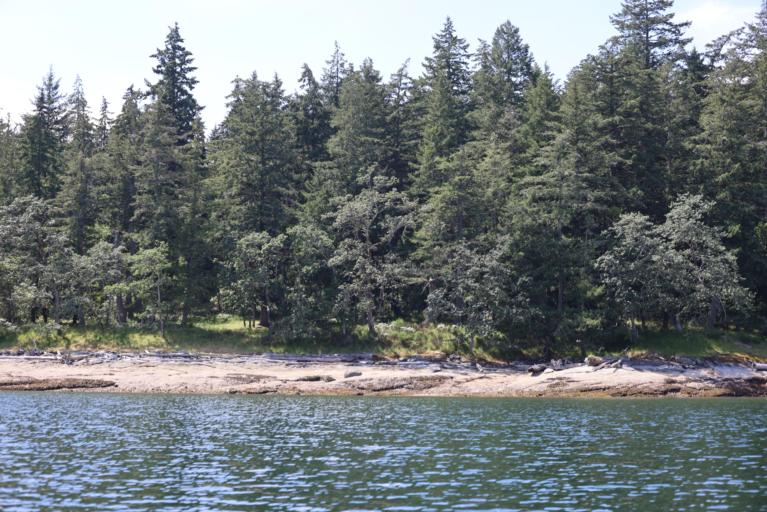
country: CA
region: British Columbia
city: Nanaimo
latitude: 49.1814
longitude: -123.9335
